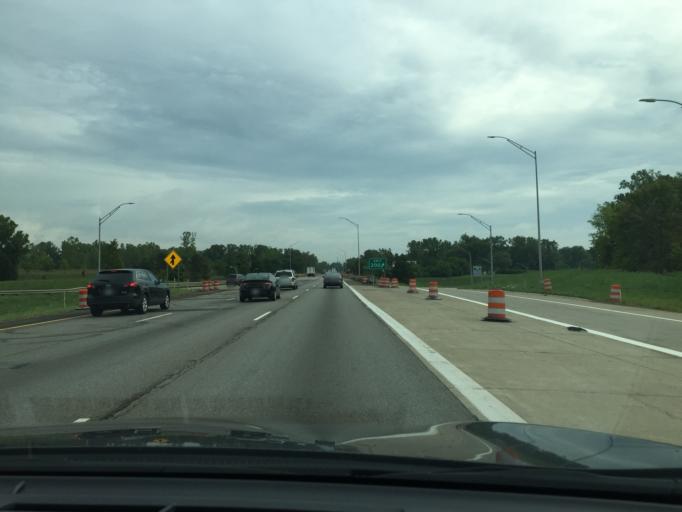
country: US
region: Michigan
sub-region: Wayne County
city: Taylor
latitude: 42.2528
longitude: -83.2998
